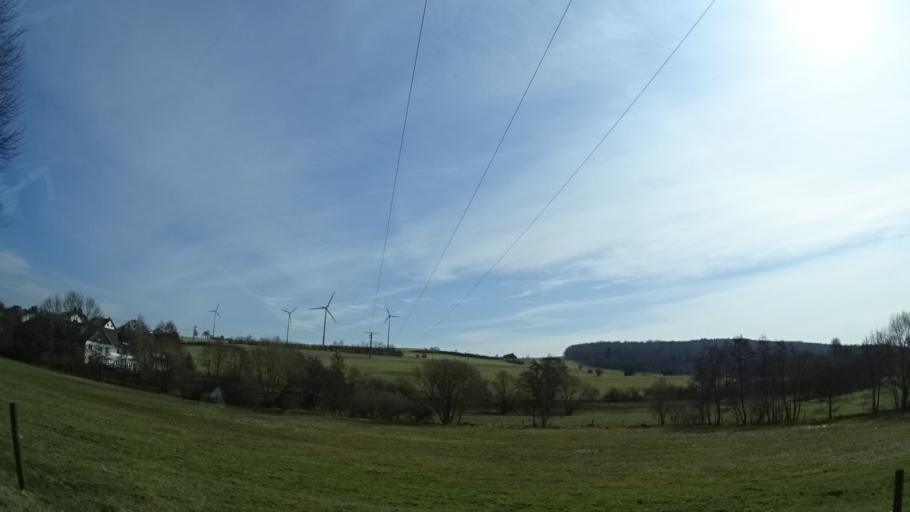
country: DE
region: Hesse
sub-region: Regierungsbezirk Giessen
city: Schwalmtal
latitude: 50.6594
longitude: 9.2697
